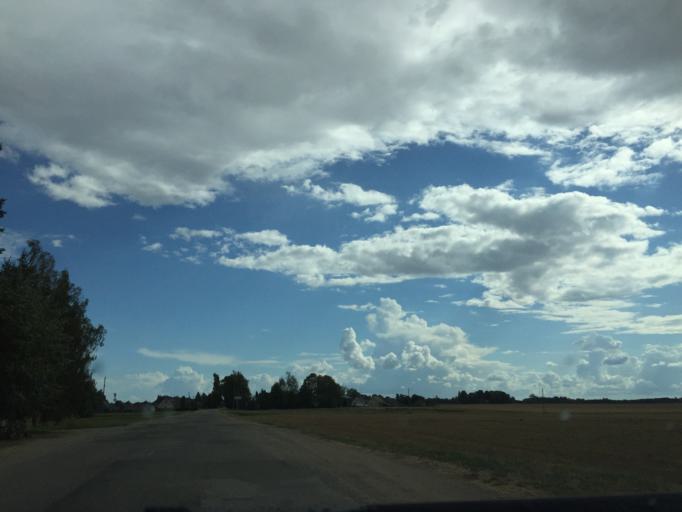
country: LT
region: Siauliu apskritis
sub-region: Joniskis
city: Joniskis
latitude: 56.3114
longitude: 23.5528
